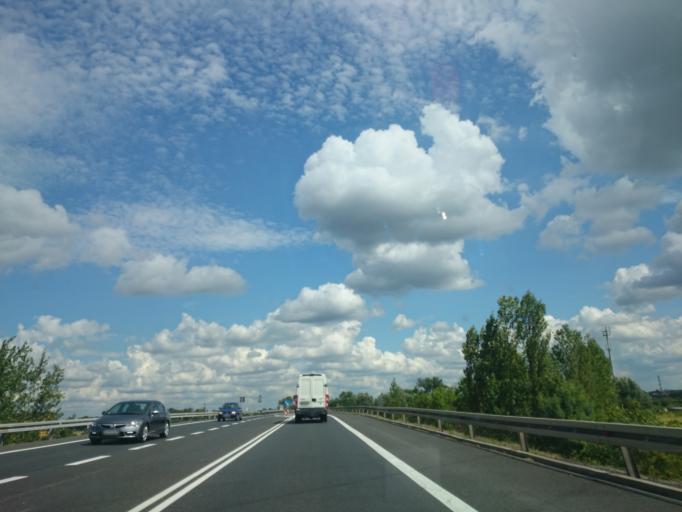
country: PL
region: Lower Silesian Voivodeship
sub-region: Legnica
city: Legnica
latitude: 51.2194
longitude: 16.1336
